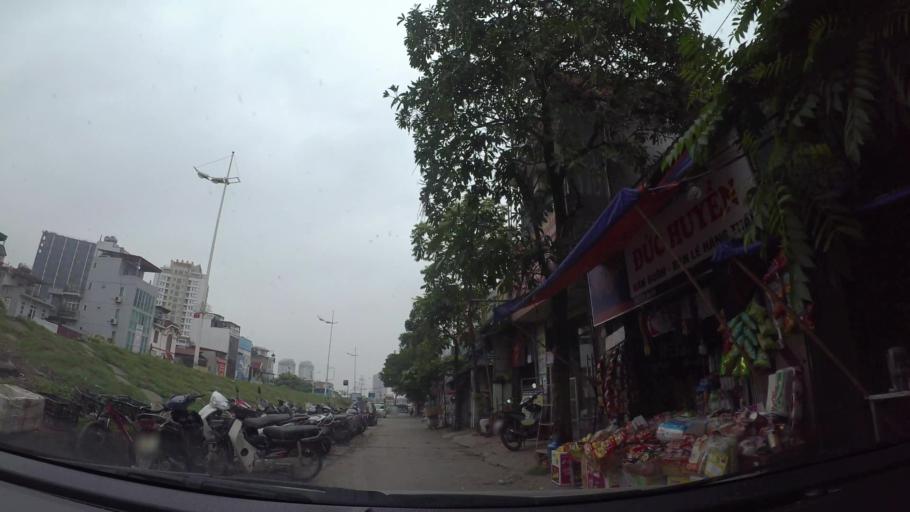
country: VN
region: Ha Noi
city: Tay Ho
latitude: 21.0799
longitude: 105.8198
